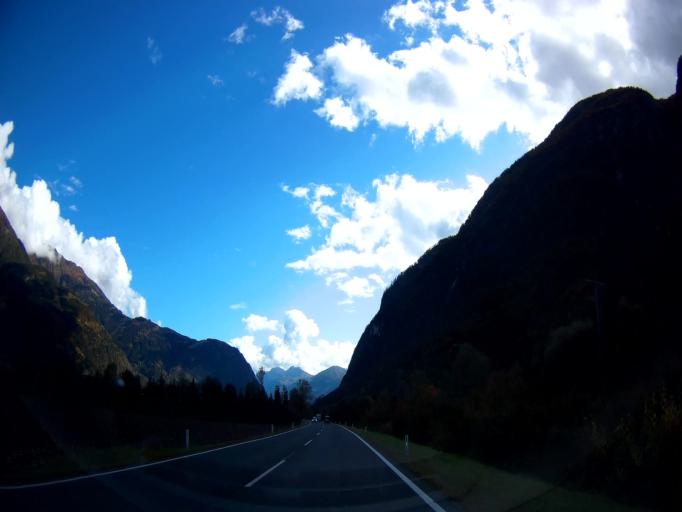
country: AT
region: Tyrol
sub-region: Politischer Bezirk Lienz
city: Nikolsdorf
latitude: 46.7852
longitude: 12.8821
